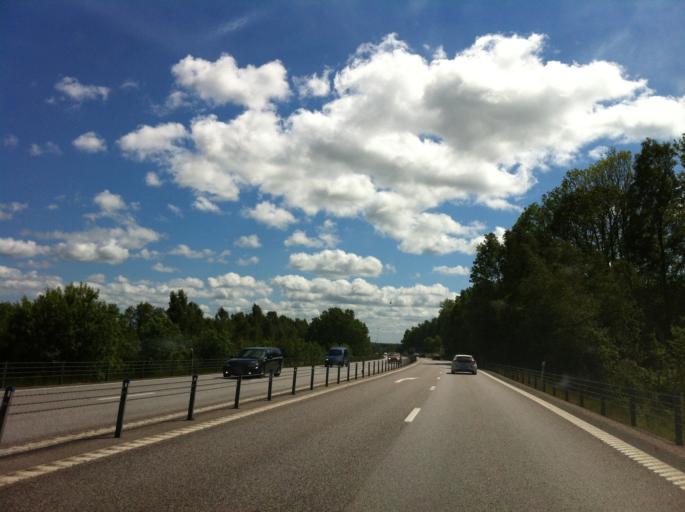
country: SE
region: Vaestra Goetaland
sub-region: Trollhattan
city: Trollhattan
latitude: 58.3284
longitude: 12.2979
